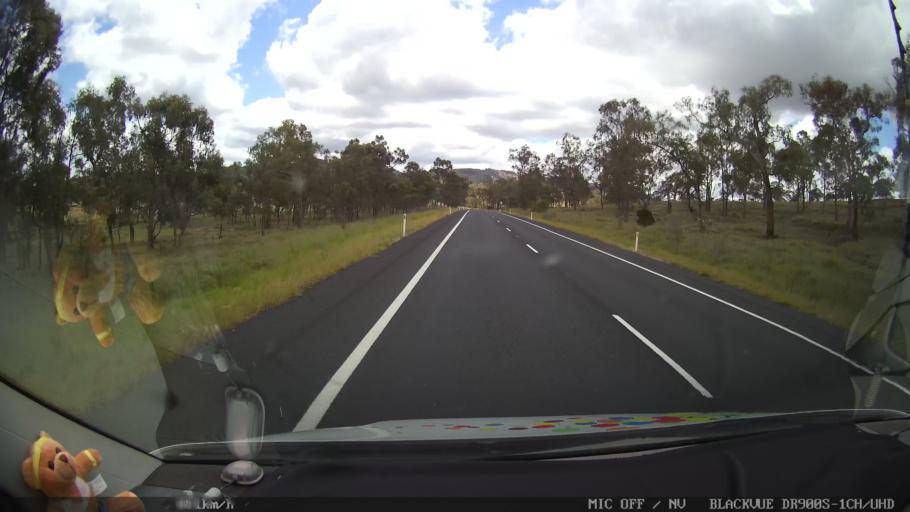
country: AU
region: New South Wales
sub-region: Glen Innes Severn
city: Glen Innes
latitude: -29.3707
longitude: 151.8948
